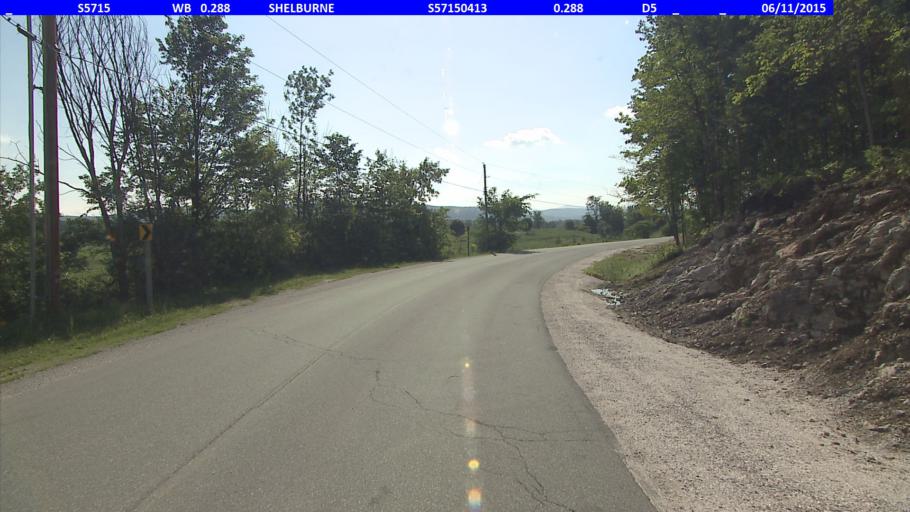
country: US
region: Vermont
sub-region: Chittenden County
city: Hinesburg
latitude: 44.3653
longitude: -73.1663
